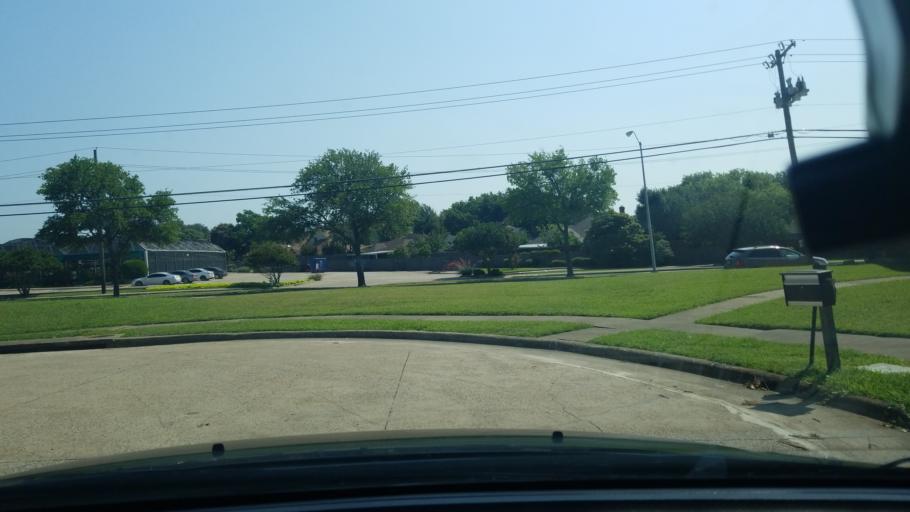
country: US
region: Texas
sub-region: Dallas County
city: Mesquite
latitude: 32.8215
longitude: -96.6200
